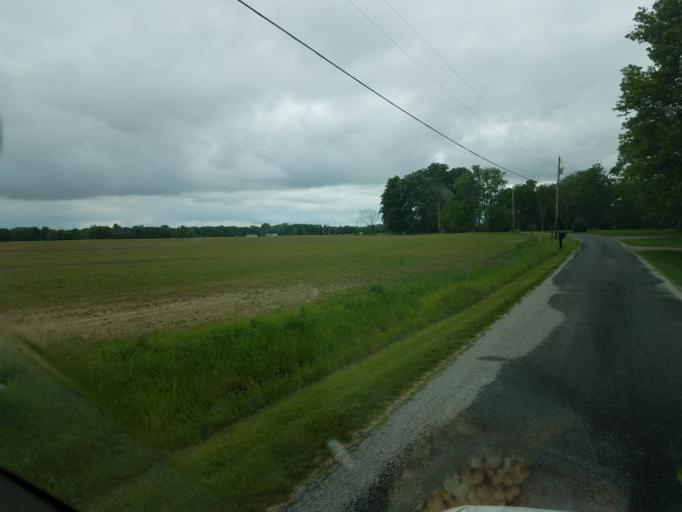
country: US
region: Ohio
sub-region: Marion County
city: Marion
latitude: 40.5228
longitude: -83.0427
